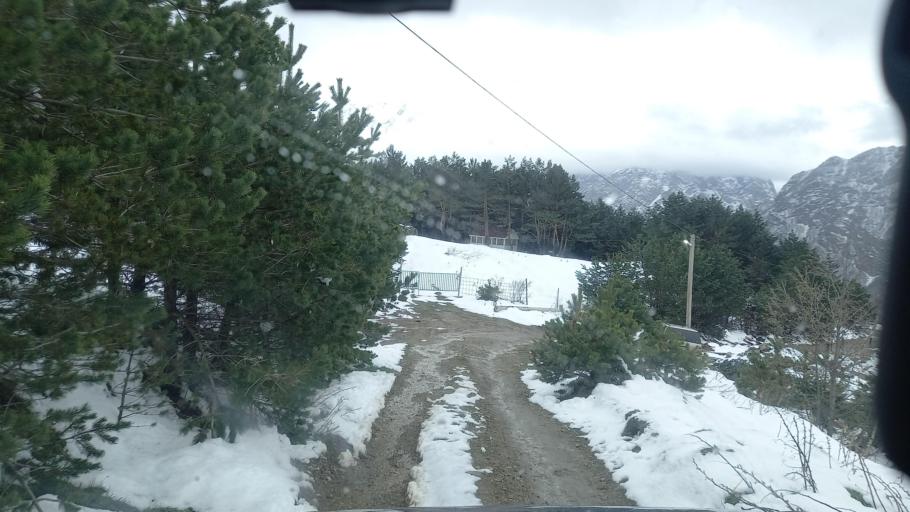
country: RU
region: North Ossetia
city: Mizur
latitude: 42.8102
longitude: 43.9564
